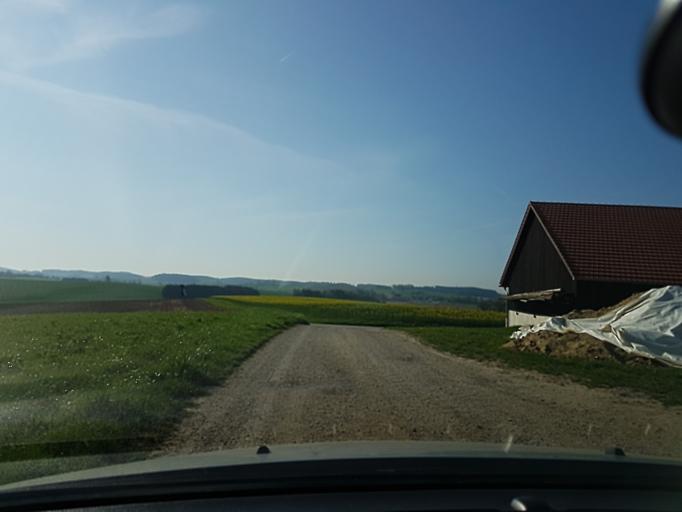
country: DE
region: Bavaria
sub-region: Lower Bavaria
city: Vilsheim
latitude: 48.4634
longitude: 12.1286
